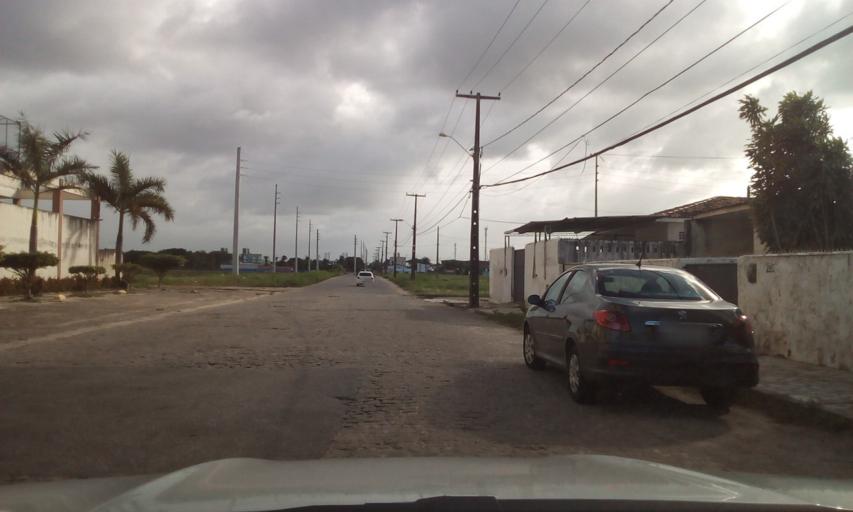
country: BR
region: Paraiba
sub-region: Joao Pessoa
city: Joao Pessoa
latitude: -7.0772
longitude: -34.8433
